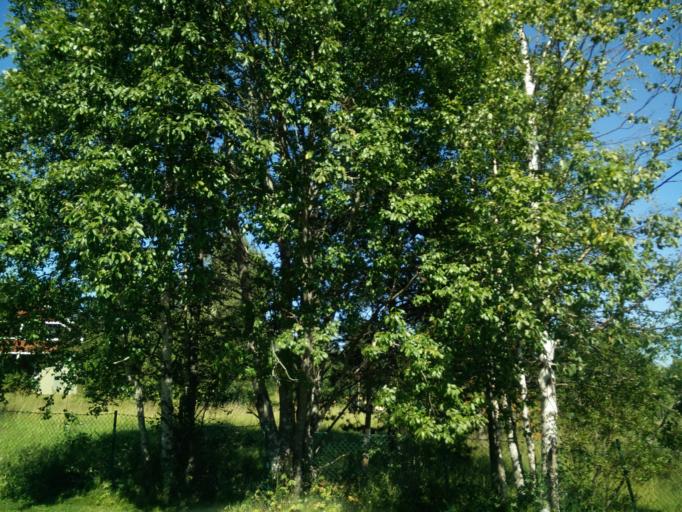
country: SE
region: Jaemtland
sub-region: Bergs Kommun
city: Hoverberg
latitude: 62.7679
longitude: 14.4289
